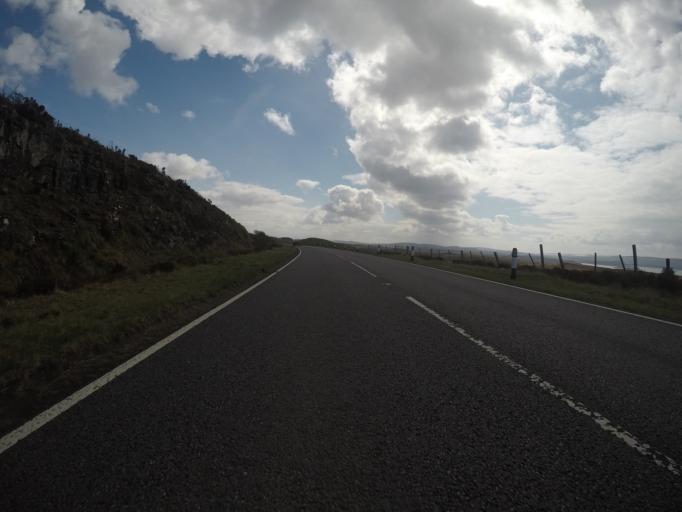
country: GB
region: Scotland
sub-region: Highland
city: Portree
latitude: 57.5524
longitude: -6.3657
